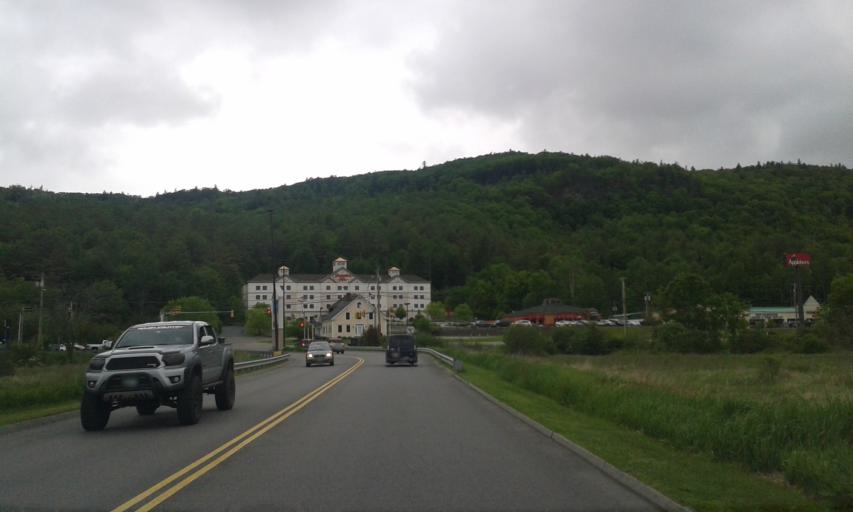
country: US
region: New Hampshire
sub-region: Grafton County
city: Littleton
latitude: 44.3049
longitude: -71.8018
